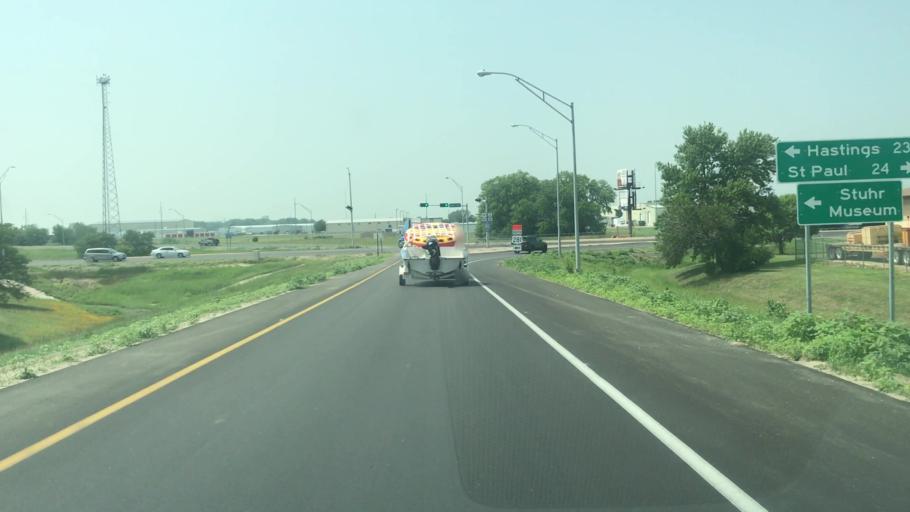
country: US
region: Nebraska
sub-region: Hall County
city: Grand Island
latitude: 40.9150
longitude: -98.3819
